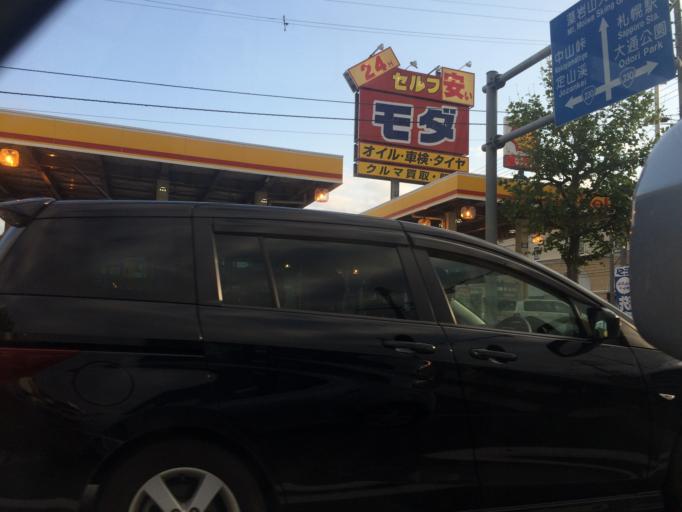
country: JP
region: Hokkaido
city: Sapporo
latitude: 43.0101
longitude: 141.3455
